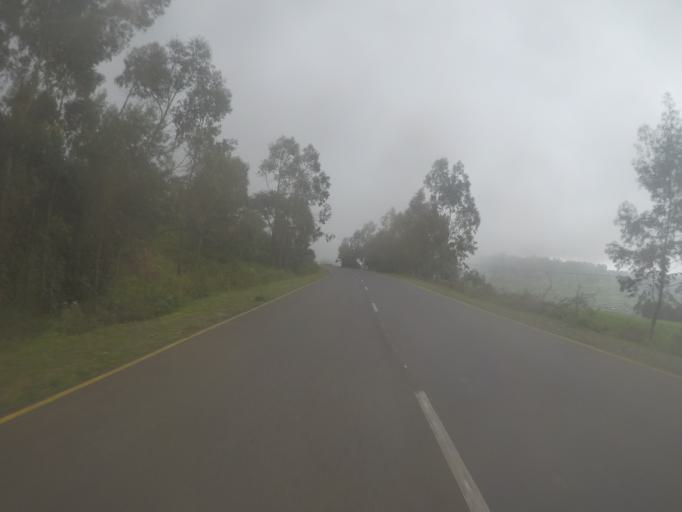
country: ET
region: Amhara
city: Gondar
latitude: 12.7428
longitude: 37.5204
